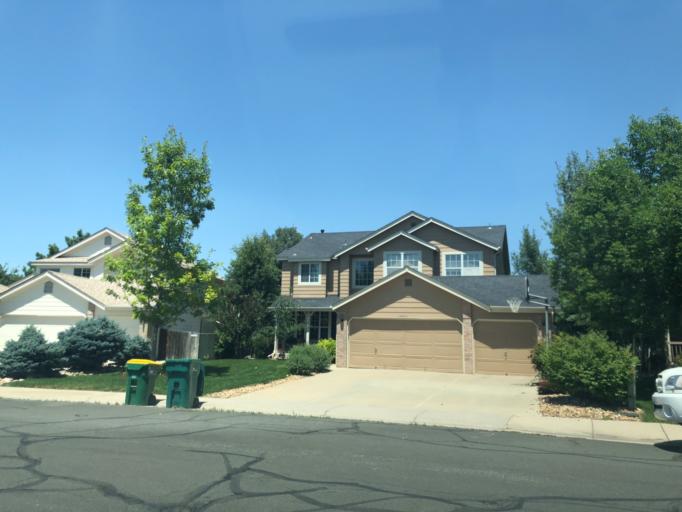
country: US
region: Colorado
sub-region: Arapahoe County
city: Dove Valley
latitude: 39.6316
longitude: -104.7667
